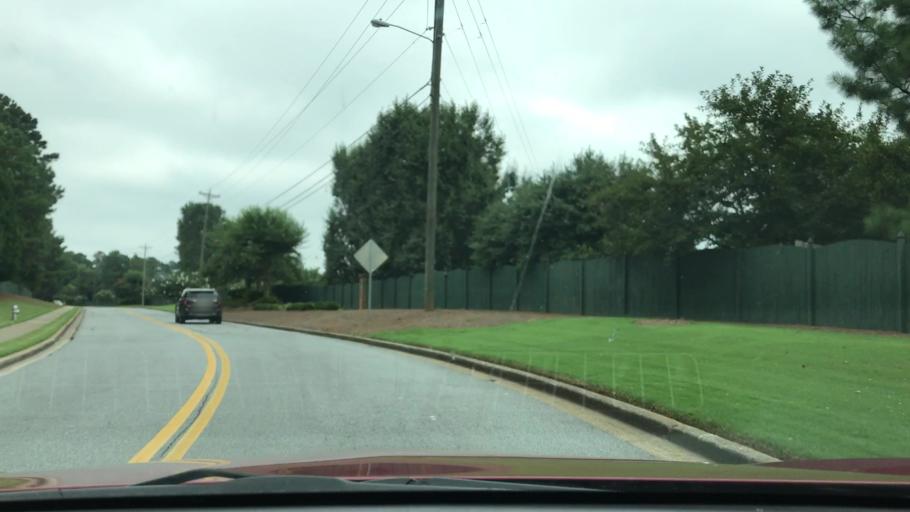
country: US
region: Georgia
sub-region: Gwinnett County
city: Lawrenceville
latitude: 34.0077
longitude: -84.0246
